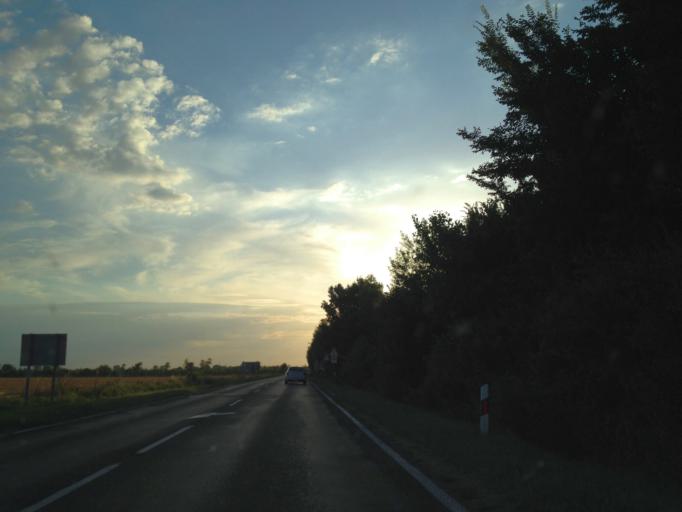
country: HU
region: Gyor-Moson-Sopron
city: Kimle
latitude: 47.8134
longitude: 17.3525
